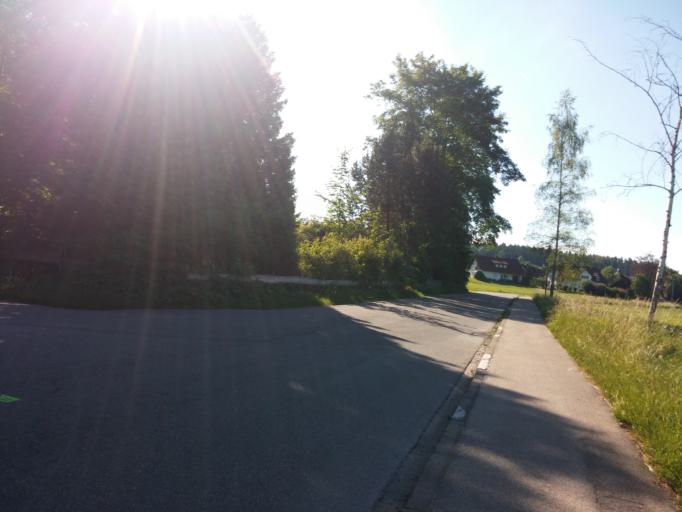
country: DE
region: Baden-Wuerttemberg
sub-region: Tuebingen Region
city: Kisslegg
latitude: 47.7823
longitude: 9.8765
